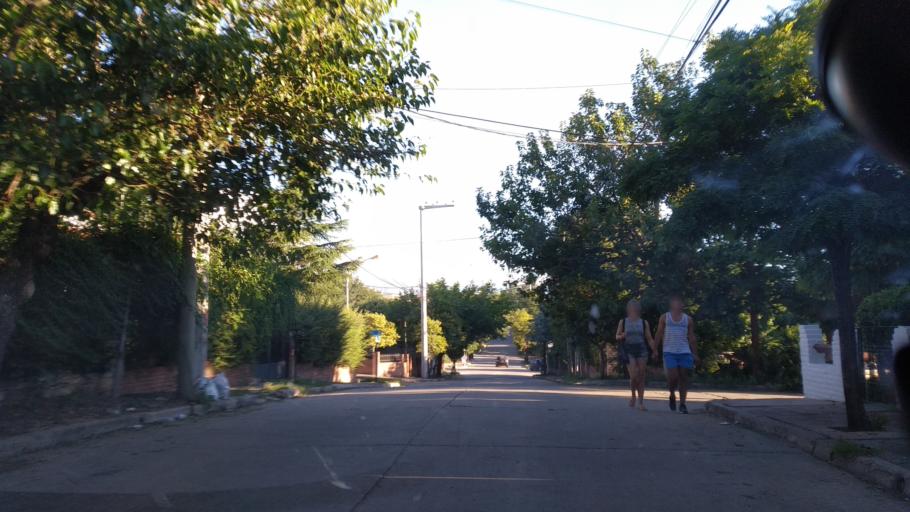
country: AR
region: Cordoba
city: Mina Clavero
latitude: -31.7173
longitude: -65.0032
